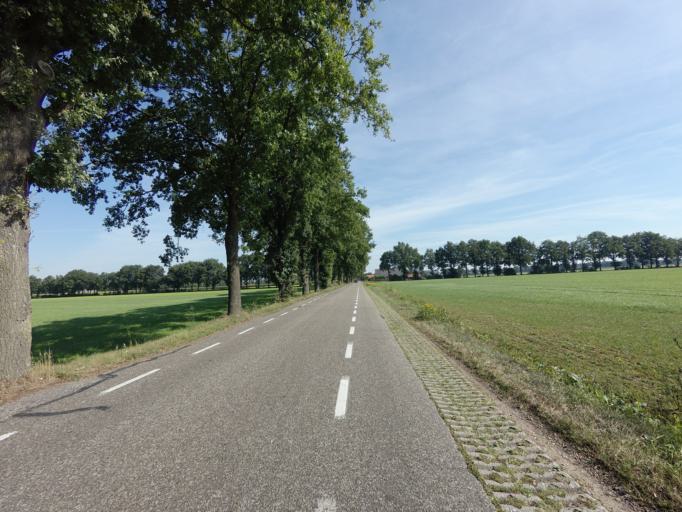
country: NL
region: Gelderland
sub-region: Oost Gelre
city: Lichtenvoorde
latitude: 52.0384
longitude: 6.5416
